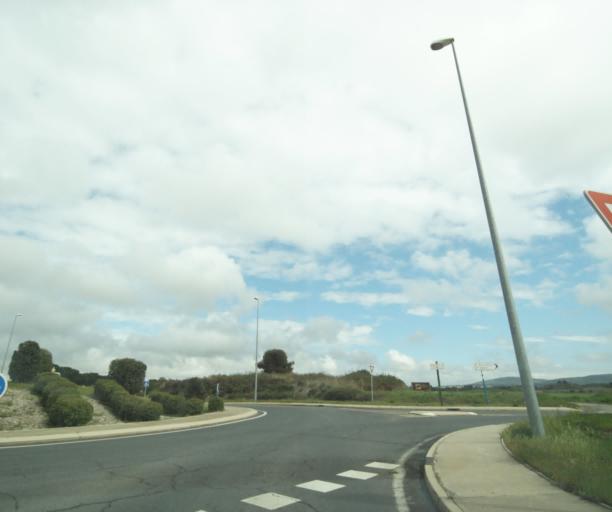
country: FR
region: Languedoc-Roussillon
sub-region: Departement de l'Herault
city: Pignan
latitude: 43.5783
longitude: 3.7559
